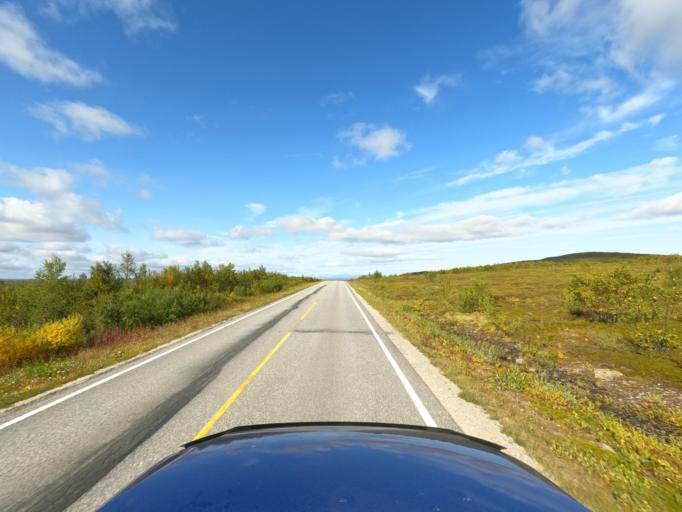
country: NO
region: Finnmark Fylke
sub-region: Karasjok
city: Karasjohka
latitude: 69.5571
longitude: 25.3981
